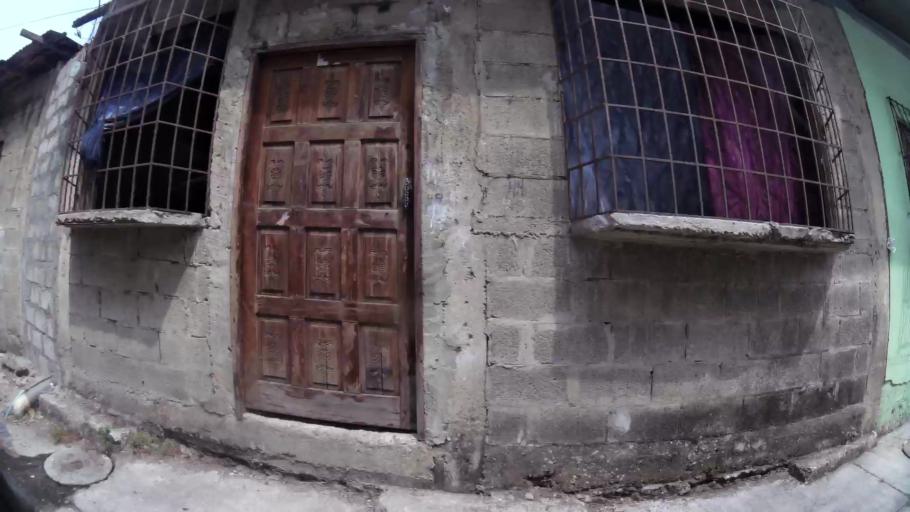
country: EC
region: Guayas
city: Guayaquil
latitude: -2.2302
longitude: -79.9056
